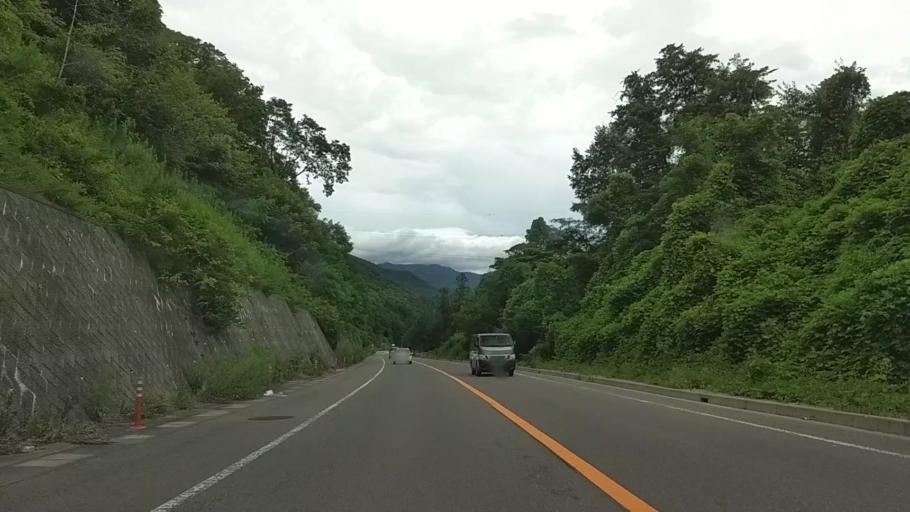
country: JP
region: Yamanashi
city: Otsuki
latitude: 35.5599
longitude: 138.9368
